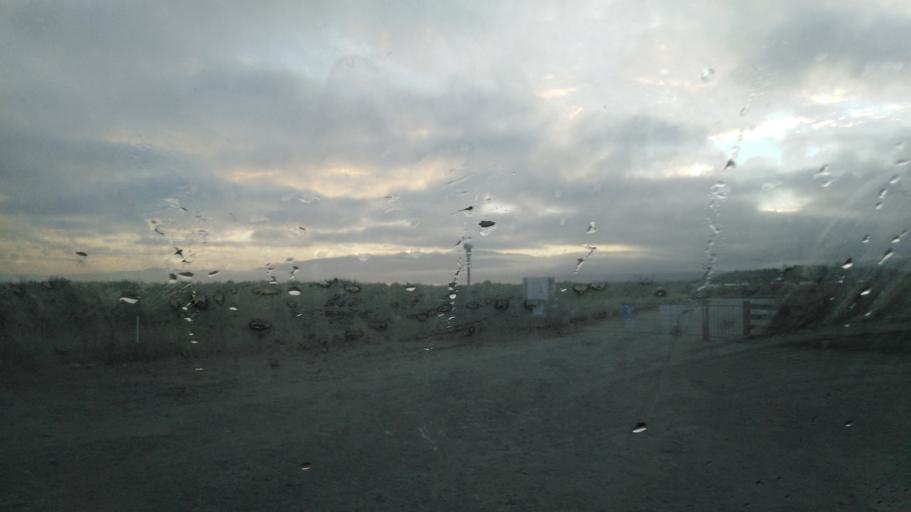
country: NZ
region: West Coast
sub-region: Buller District
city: Westport
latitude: -41.7340
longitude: 171.6038
